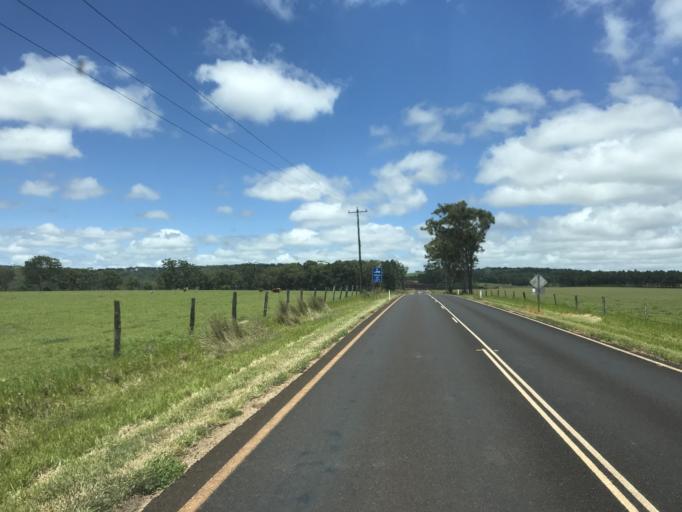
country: AU
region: Queensland
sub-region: Tablelands
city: Ravenshoe
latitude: -17.5120
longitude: 145.4522
